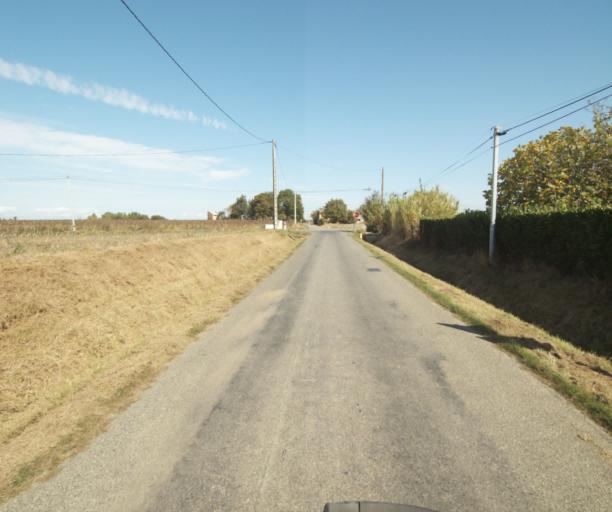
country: FR
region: Midi-Pyrenees
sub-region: Departement du Tarn-et-Garonne
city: Verdun-sur-Garonne
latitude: 43.8552
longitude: 1.2097
